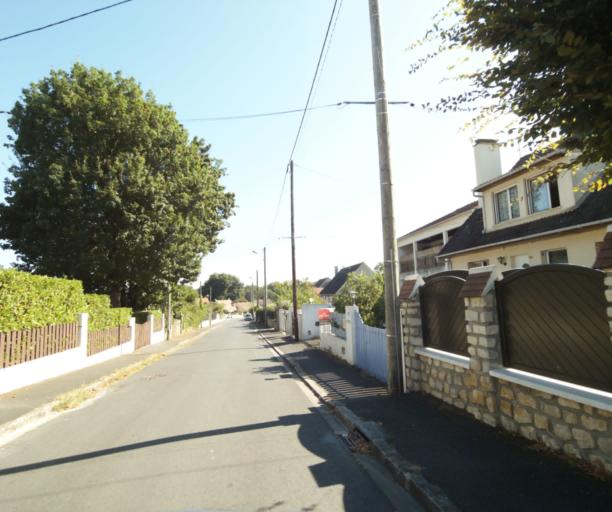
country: FR
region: Ile-de-France
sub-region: Departement de l'Essonne
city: Saint-Vrain
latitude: 48.5342
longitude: 2.3505
